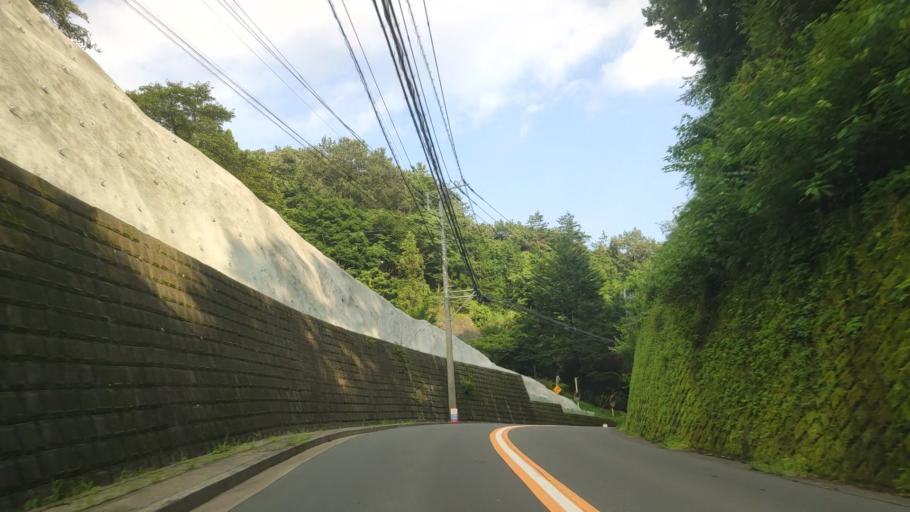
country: JP
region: Saitama
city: Hanno
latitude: 35.8271
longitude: 139.2732
